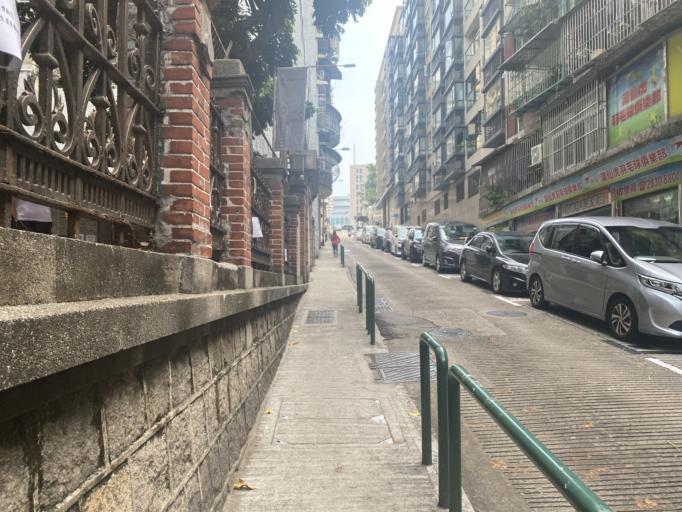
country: MO
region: Macau
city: Macau
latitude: 22.1966
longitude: 113.5477
